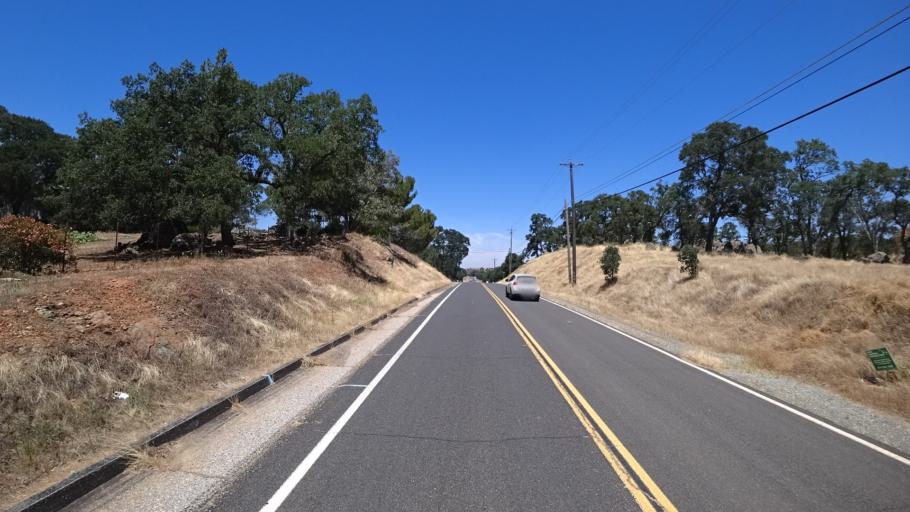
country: US
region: California
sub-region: Calaveras County
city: Rancho Calaveras
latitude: 38.1321
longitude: -120.8456
